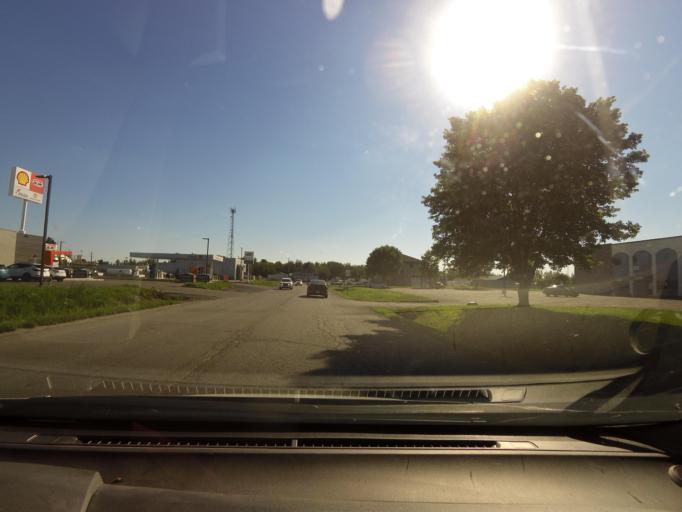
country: CA
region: Quebec
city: Sainte-Catherine
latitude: 46.2925
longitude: -72.5409
